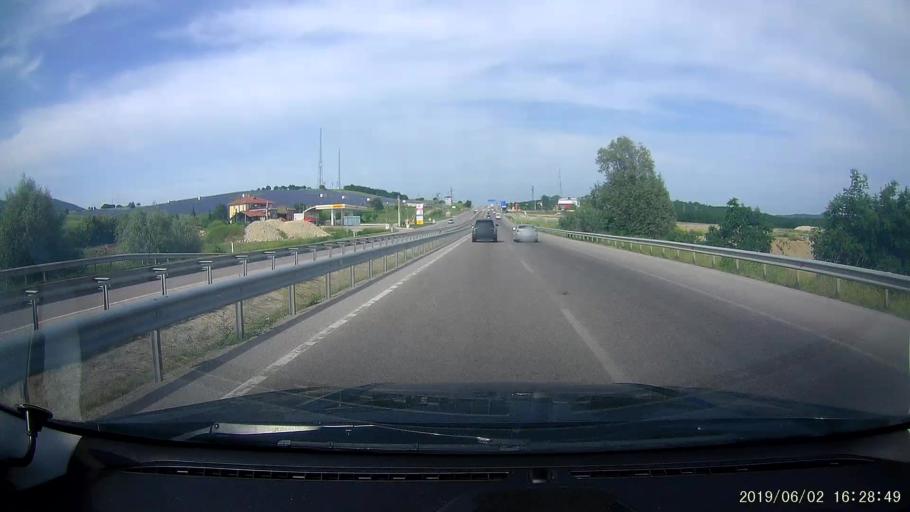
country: TR
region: Samsun
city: Ladik
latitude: 41.0086
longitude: 35.8563
